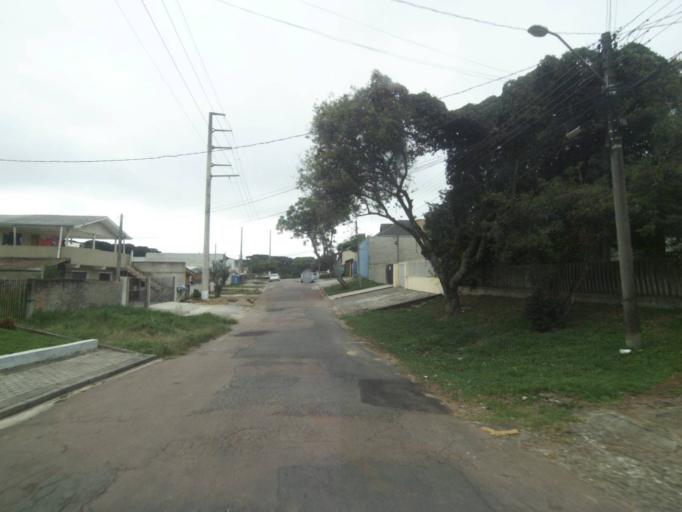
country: BR
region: Parana
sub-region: Sao Jose Dos Pinhais
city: Sao Jose dos Pinhais
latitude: -25.5392
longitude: -49.2848
